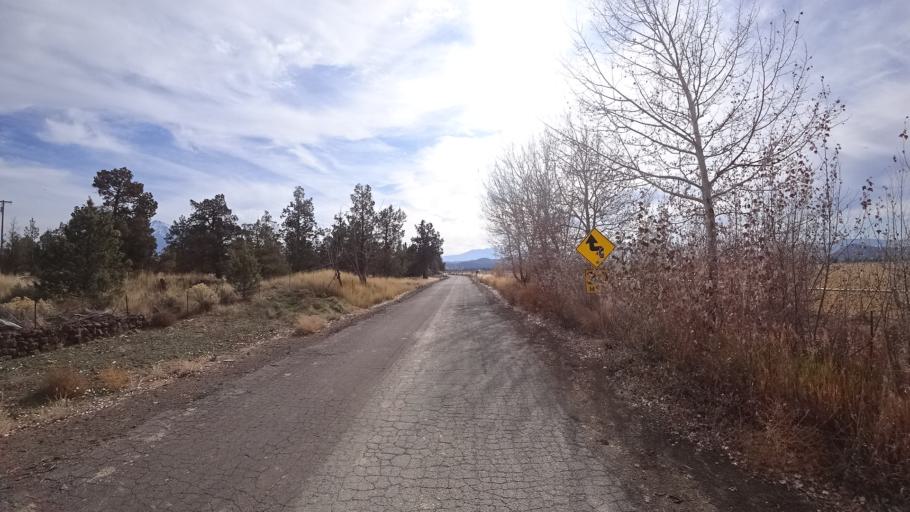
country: US
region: California
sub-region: Siskiyou County
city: Montague
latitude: 41.6069
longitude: -122.4049
